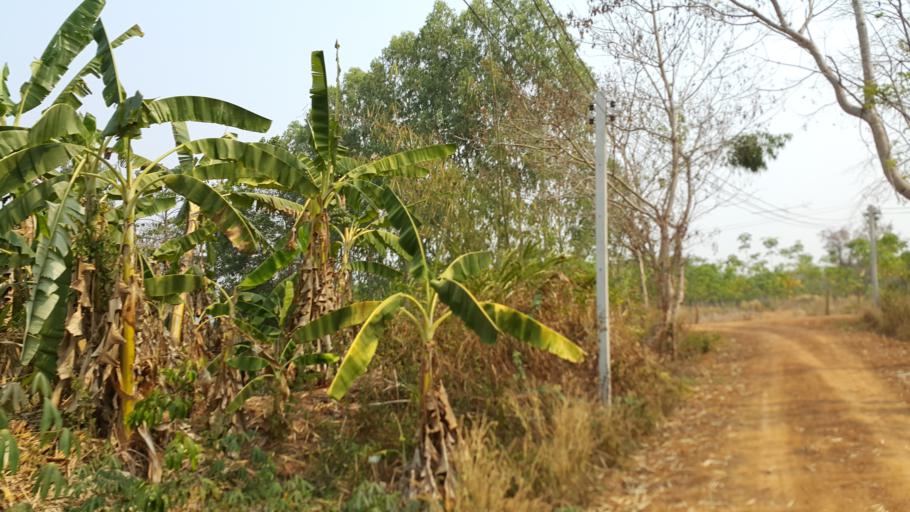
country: TH
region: Nakhon Phanom
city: Ban Phaeng
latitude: 17.8273
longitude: 104.2472
